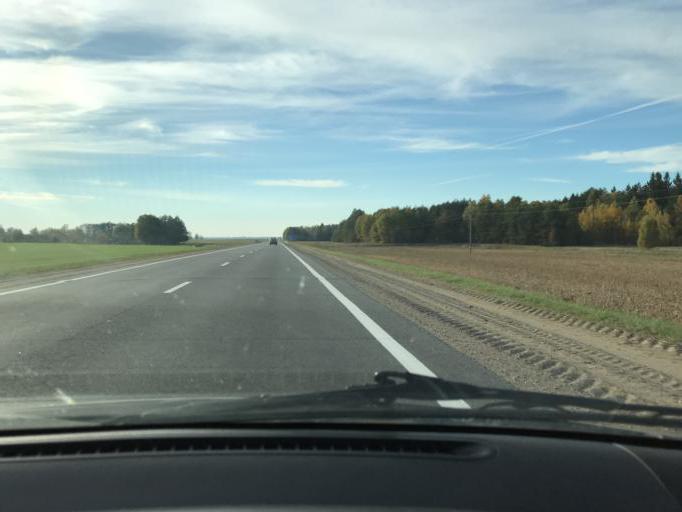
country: BY
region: Brest
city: Ivanava
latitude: 52.1563
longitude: 25.7138
